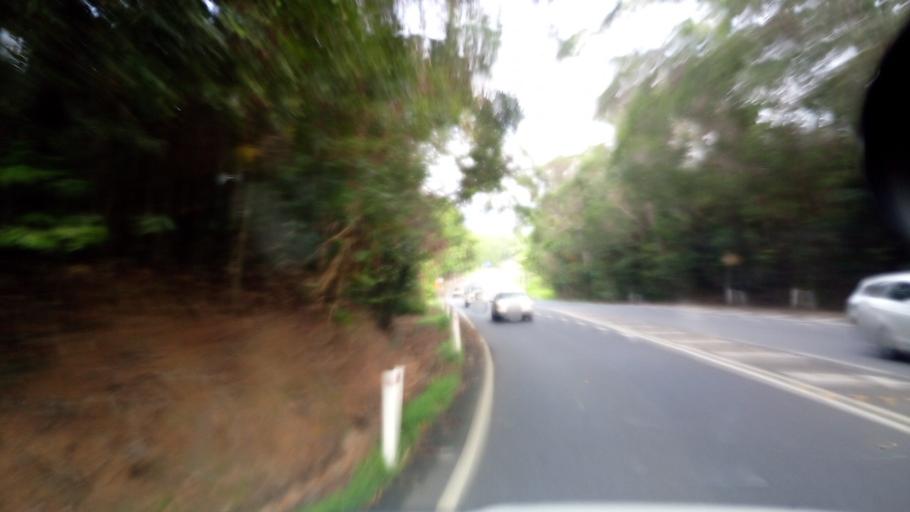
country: AU
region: Queensland
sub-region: Tablelands
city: Kuranda
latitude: -16.8189
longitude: 145.6464
